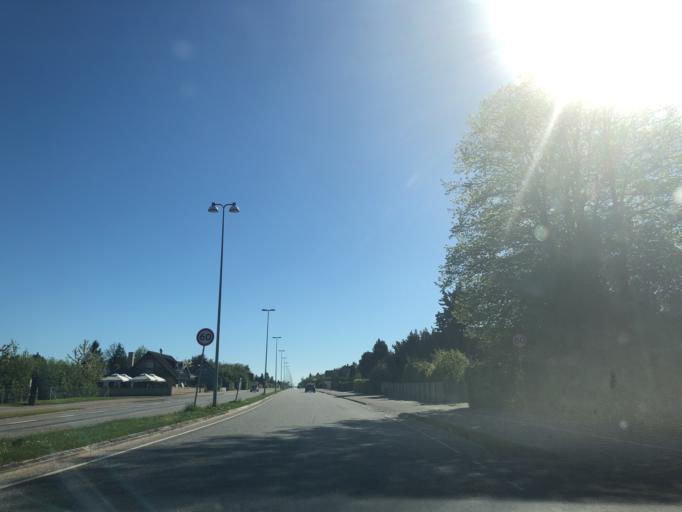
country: DK
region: Zealand
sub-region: Koge Kommune
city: Koge
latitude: 55.4421
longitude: 12.1678
